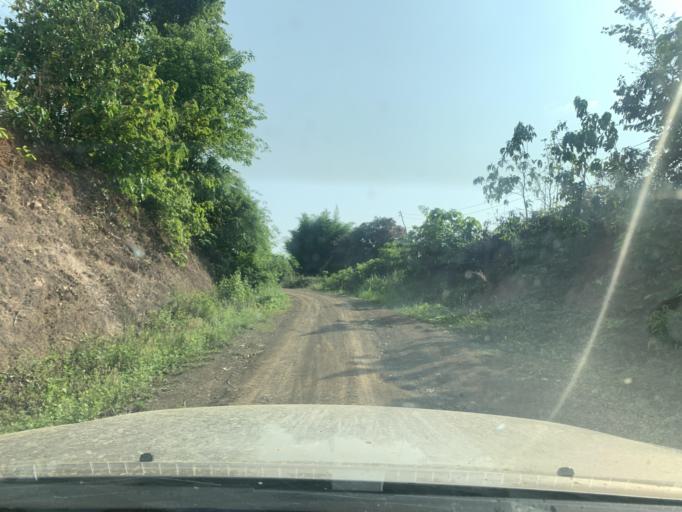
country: TH
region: Uttaradit
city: Ban Khok
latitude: 18.2844
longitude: 101.3175
